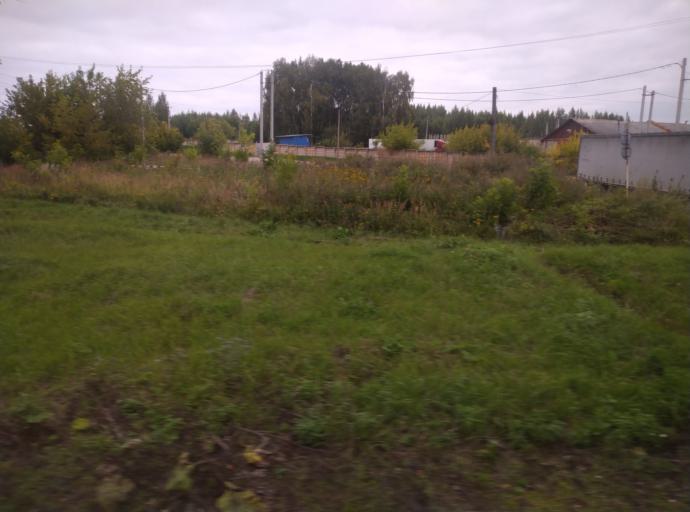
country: RU
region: Kostroma
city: Nerekhta
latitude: 57.4572
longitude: 40.5287
